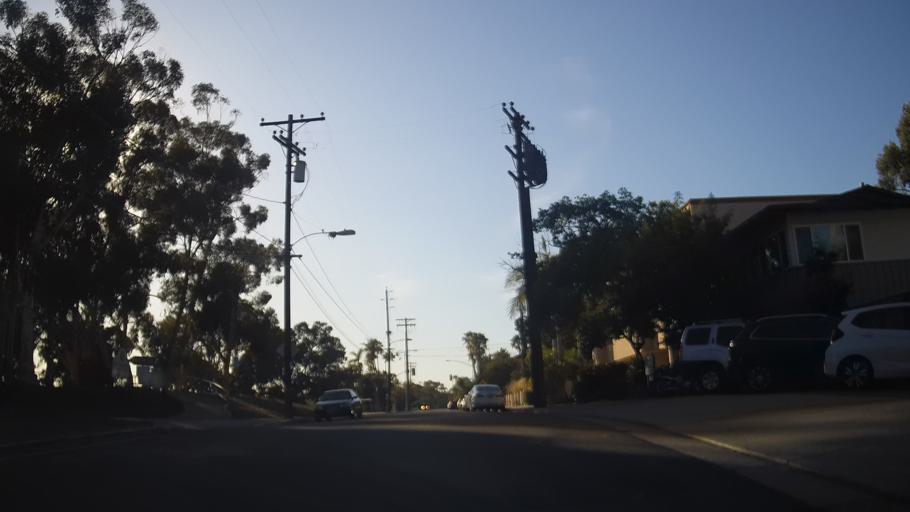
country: US
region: California
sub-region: San Diego County
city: San Diego
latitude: 32.7412
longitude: -117.1460
